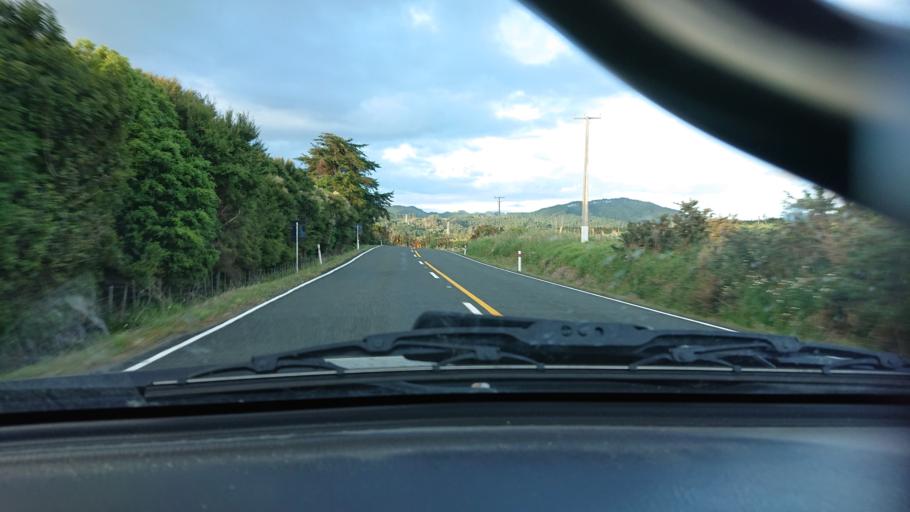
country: NZ
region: Auckland
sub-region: Auckland
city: Parakai
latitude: -36.5188
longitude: 174.4495
